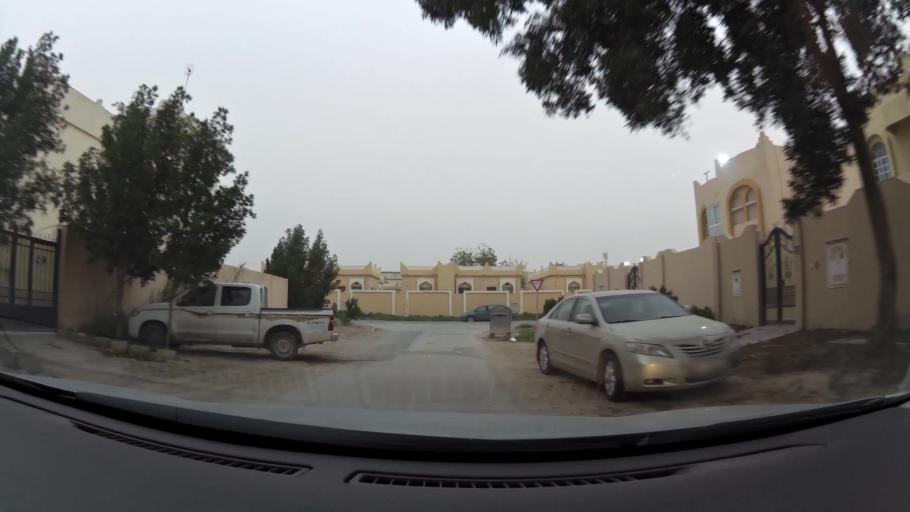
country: QA
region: Baladiyat ad Dawhah
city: Doha
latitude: 25.2363
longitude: 51.4979
